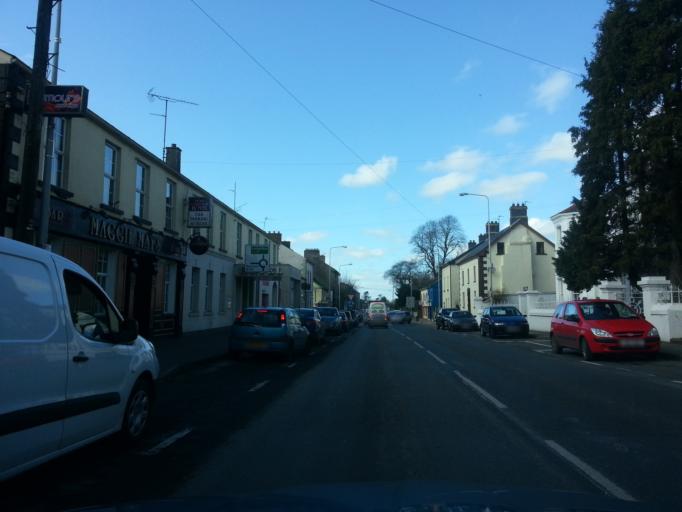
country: GB
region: Northern Ireland
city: Lisnaskea
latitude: 54.2538
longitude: -7.4442
